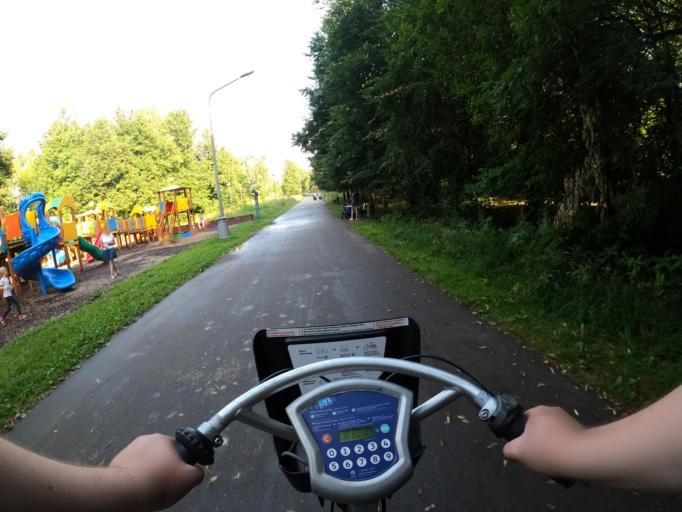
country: RU
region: Moscow
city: Strogino
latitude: 55.8190
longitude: 37.4035
